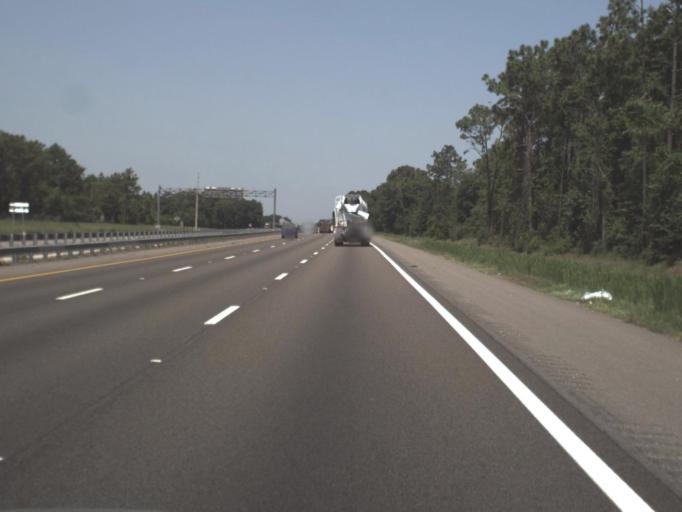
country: US
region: Florida
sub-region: Clay County
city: Bellair-Meadowbrook Terrace
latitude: 30.3146
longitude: -81.8033
